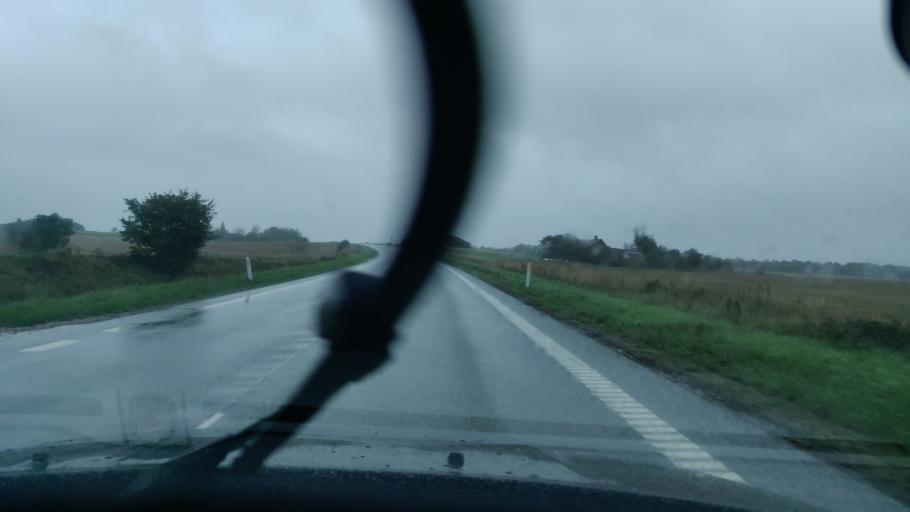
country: DK
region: North Denmark
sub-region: Thisted Kommune
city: Thisted
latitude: 56.8622
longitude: 8.5610
